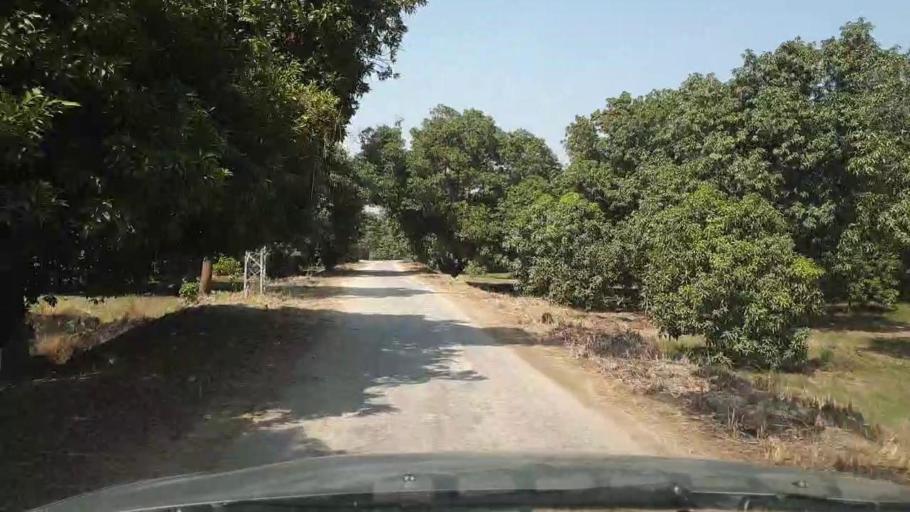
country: PK
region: Sindh
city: Tando Jam
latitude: 25.3624
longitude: 68.5143
